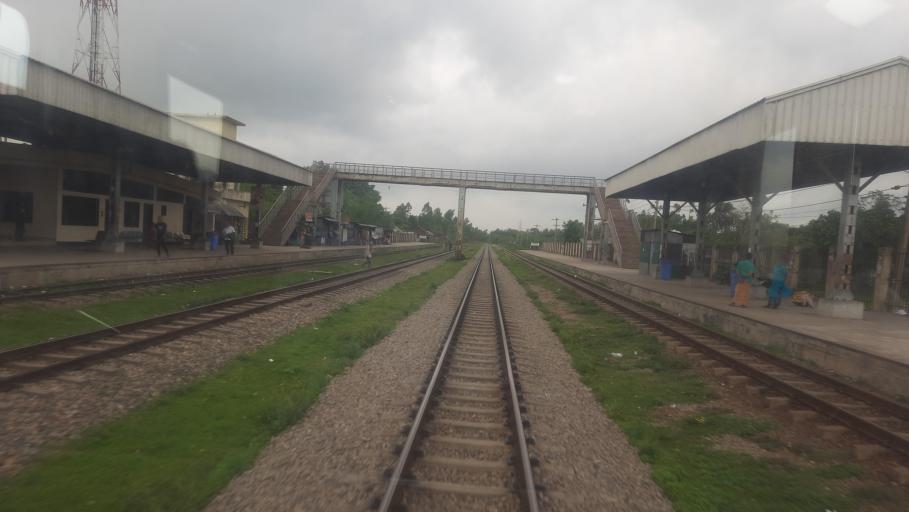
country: BD
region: Dhaka
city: Bhairab Bazar
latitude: 23.9929
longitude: 90.8671
